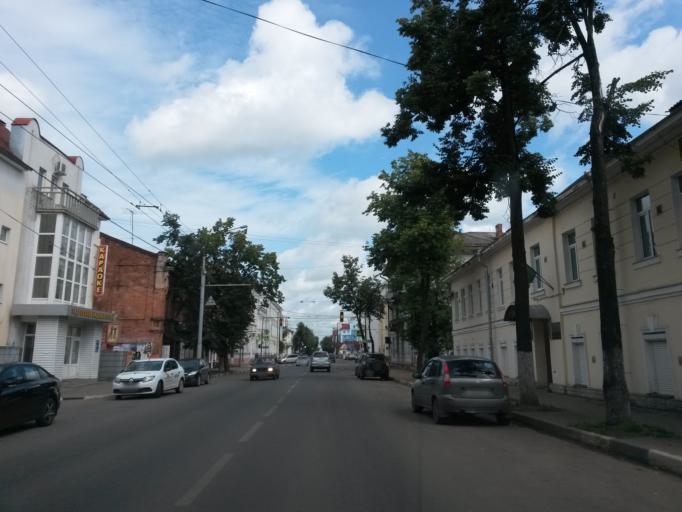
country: RU
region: Jaroslavl
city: Yaroslavl
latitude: 57.6311
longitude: 39.8796
